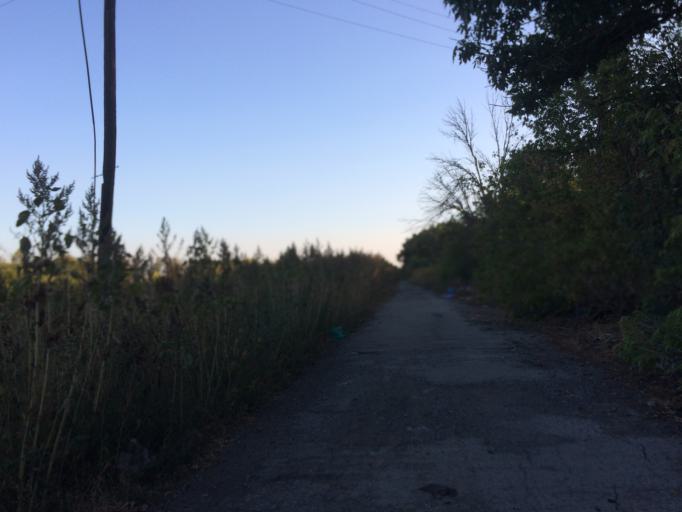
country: RU
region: Rostov
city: Gigant
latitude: 46.5176
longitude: 41.1948
